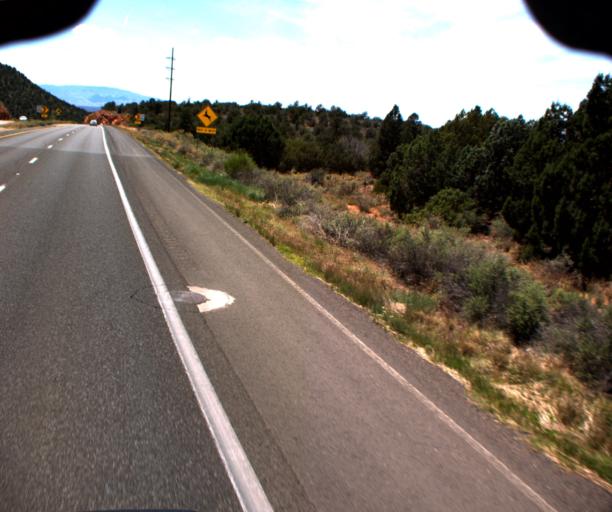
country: US
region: Arizona
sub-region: Yavapai County
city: West Sedona
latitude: 34.8485
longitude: -111.8337
